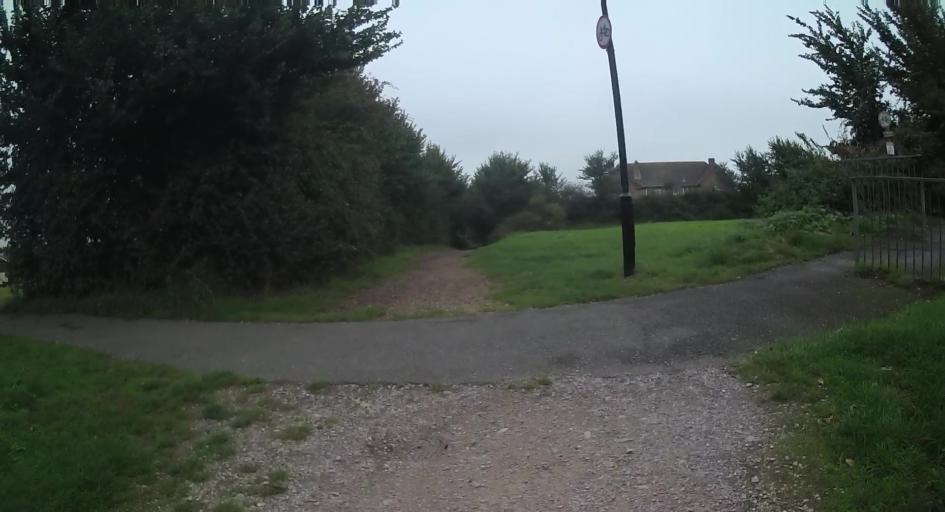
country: GB
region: England
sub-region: Isle of Wight
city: Sandown
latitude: 50.6612
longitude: -1.1584
